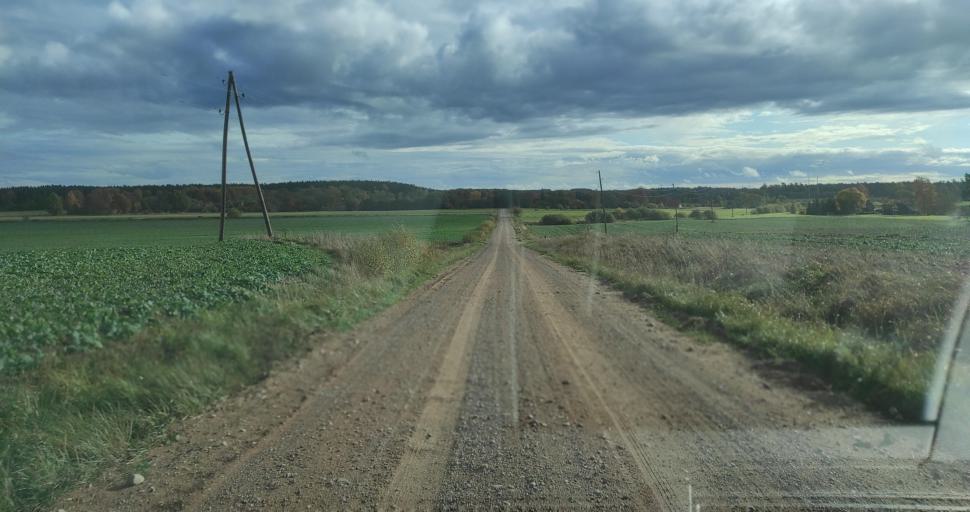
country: LV
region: Skrunda
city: Skrunda
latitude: 56.6107
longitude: 21.9660
